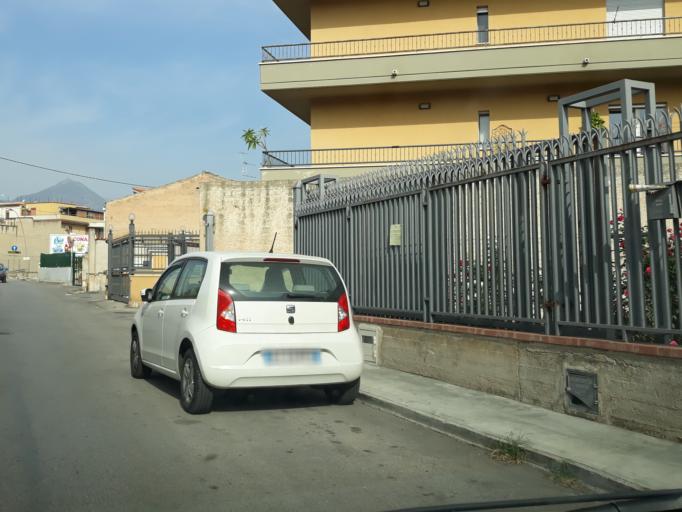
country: IT
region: Sicily
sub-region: Palermo
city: Villa Ciambra
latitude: 38.0866
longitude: 13.3456
